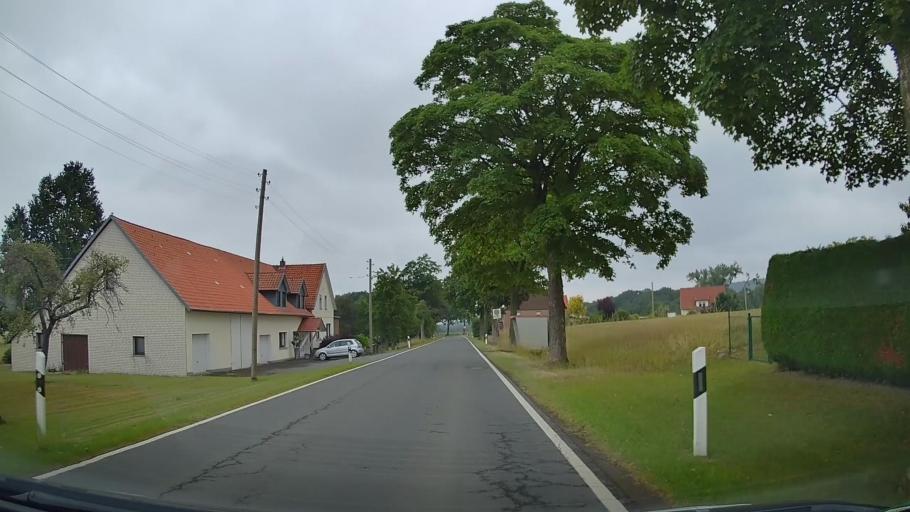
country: DE
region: Lower Saxony
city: Rinteln
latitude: 52.1441
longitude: 9.1013
